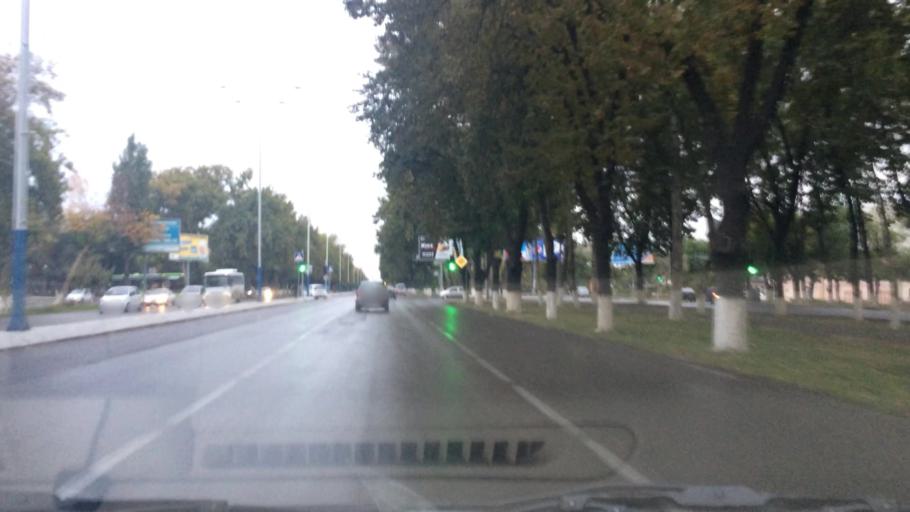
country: UZ
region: Toshkent Shahri
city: Tashkent
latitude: 41.2692
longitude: 69.2015
